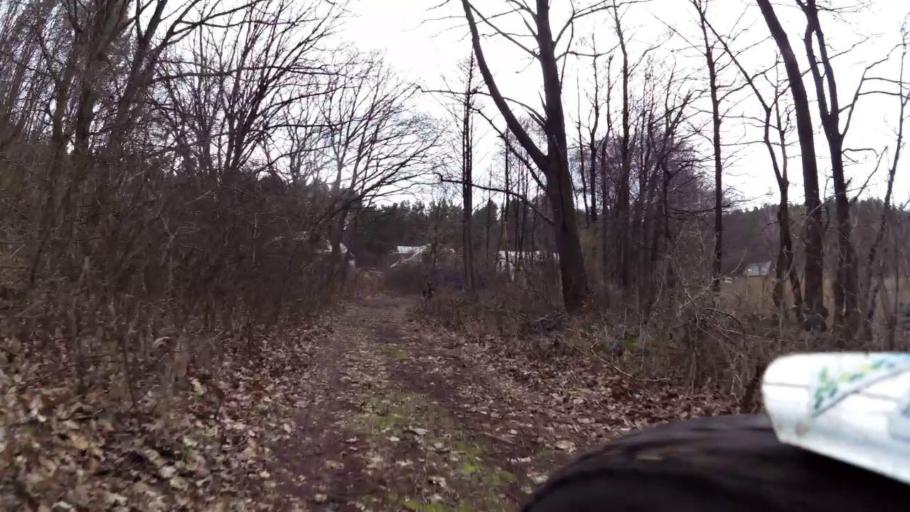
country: PL
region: West Pomeranian Voivodeship
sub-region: Powiat kamienski
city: Wolin
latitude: 53.9560
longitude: 14.5713
